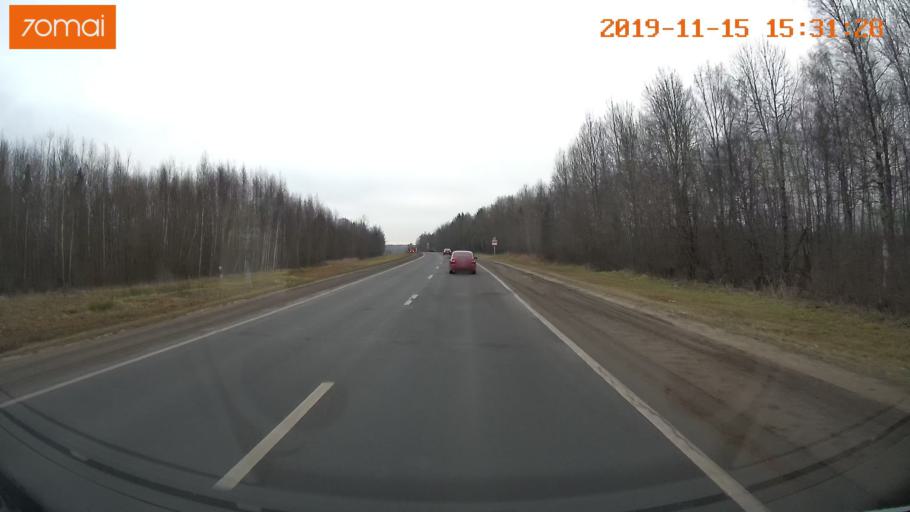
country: RU
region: Jaroslavl
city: Danilov
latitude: 58.1001
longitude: 40.1072
